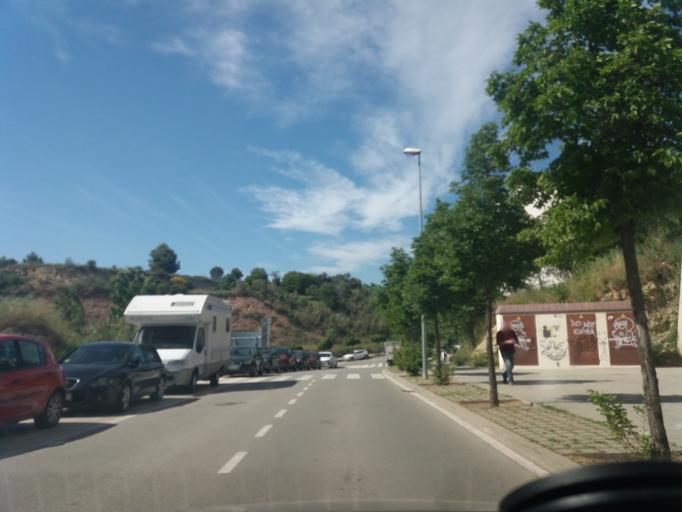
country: ES
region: Catalonia
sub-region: Provincia de Barcelona
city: Manresa
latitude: 41.7281
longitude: 1.8166
